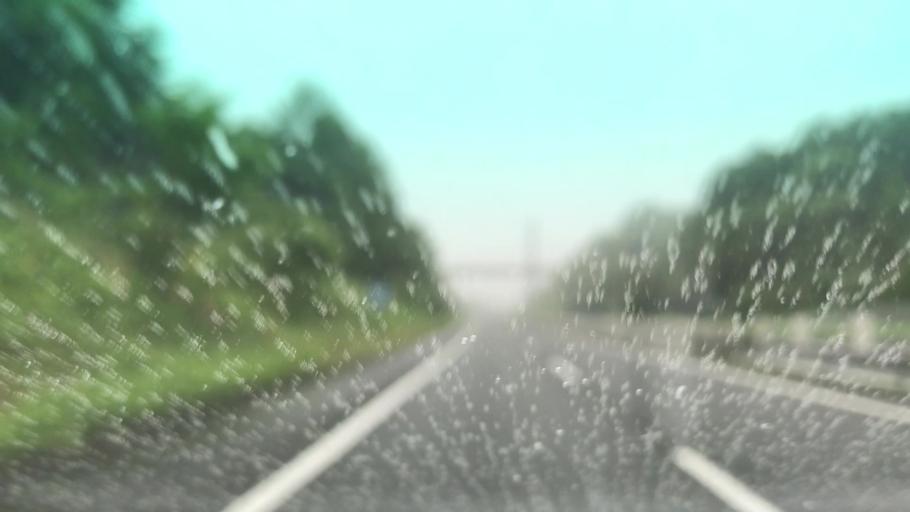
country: JP
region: Hokkaido
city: Tomakomai
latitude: 42.6277
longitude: 141.4839
